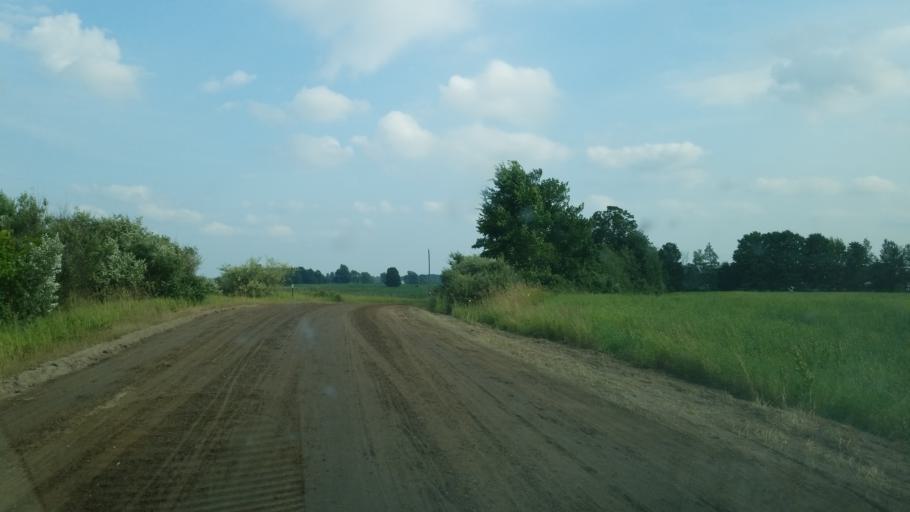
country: US
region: Michigan
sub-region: Mecosta County
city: Canadian Lakes
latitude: 43.5543
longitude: -85.3634
